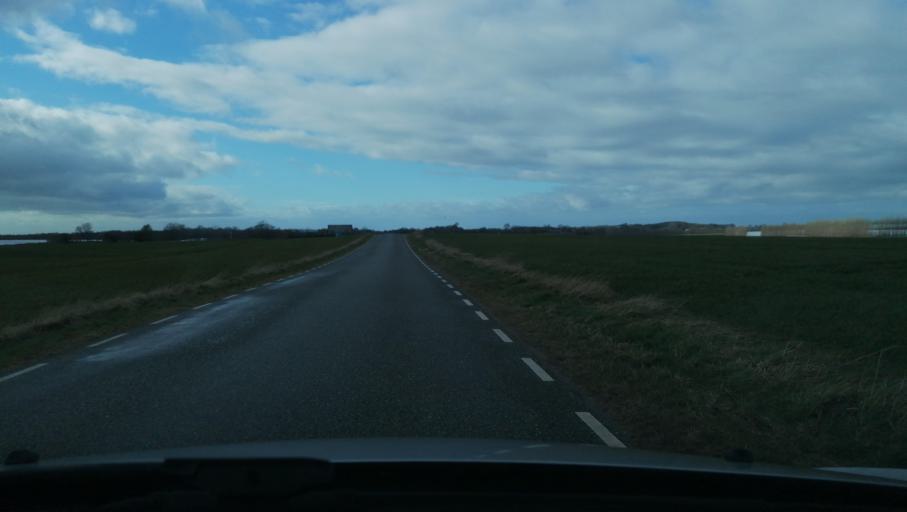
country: DK
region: Zealand
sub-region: Odsherred Kommune
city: Horve
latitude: 55.7436
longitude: 11.3917
